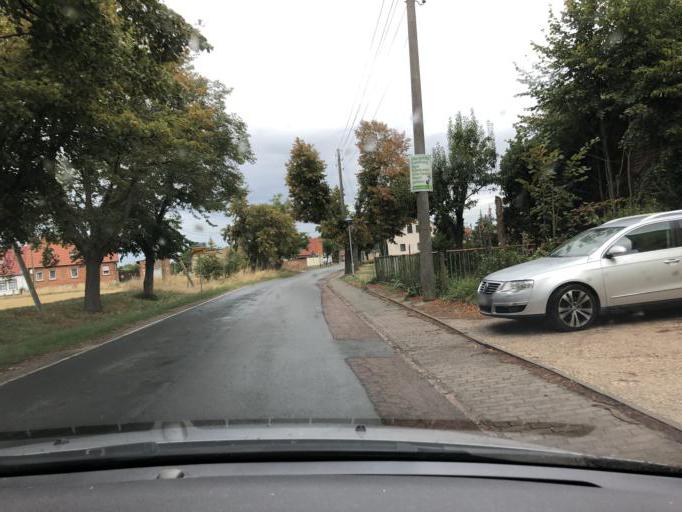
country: DE
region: Saxony-Anhalt
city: Wulfen
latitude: 51.8381
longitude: 11.8829
